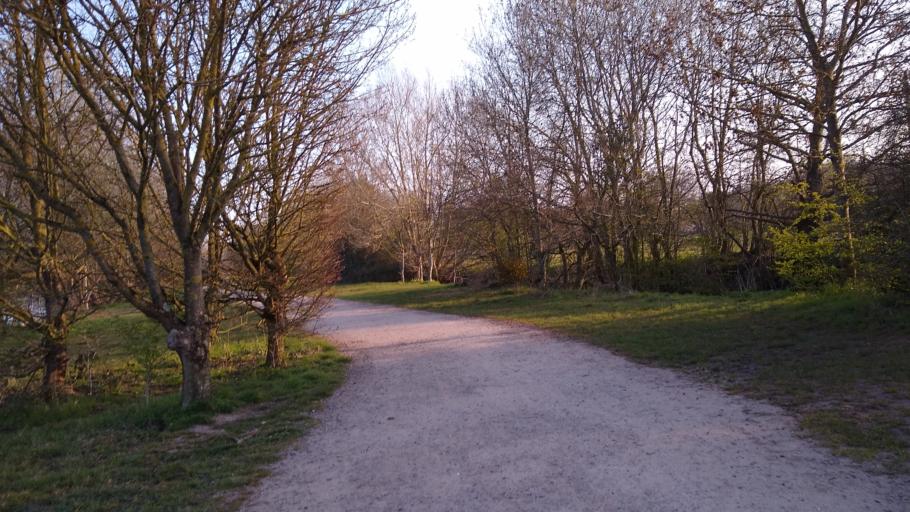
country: GB
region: England
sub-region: Wokingham
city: Woodley
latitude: 51.4449
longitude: -0.8713
